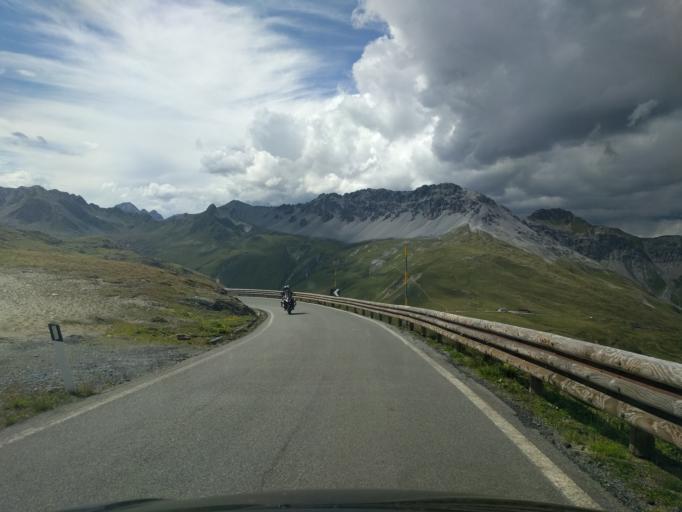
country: IT
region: Lombardy
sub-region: Provincia di Sondrio
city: Sant'Antonio
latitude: 46.5331
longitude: 10.4456
